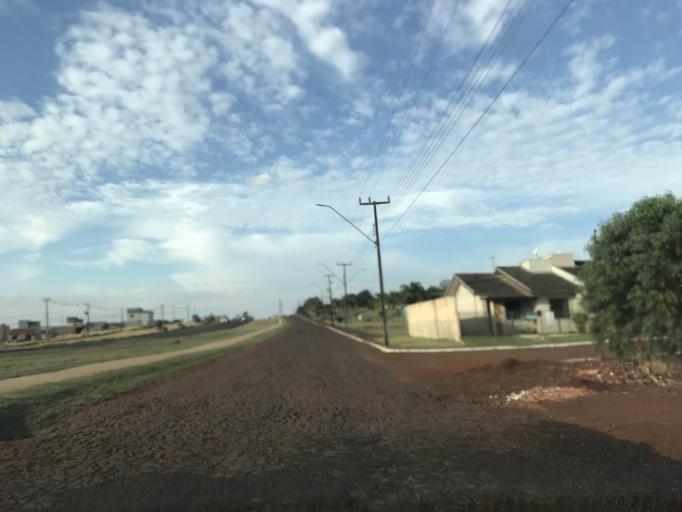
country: BR
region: Parana
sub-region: Cascavel
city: Cascavel
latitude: -25.0488
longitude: -53.6144
